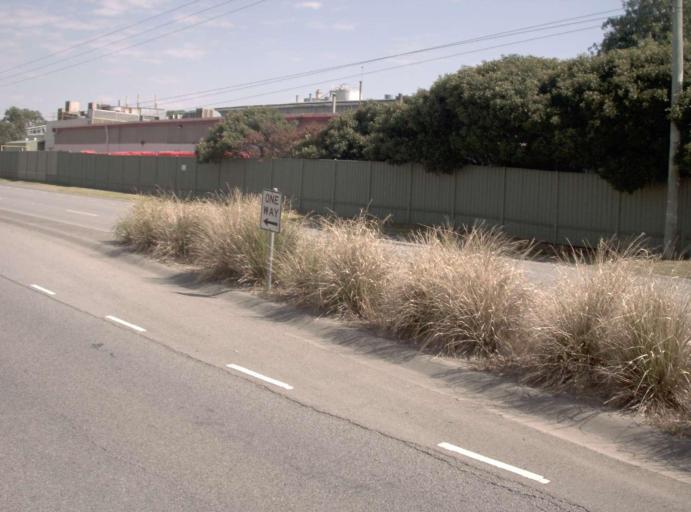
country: AU
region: Victoria
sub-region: Casey
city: Doveton
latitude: -38.0167
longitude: 145.2319
